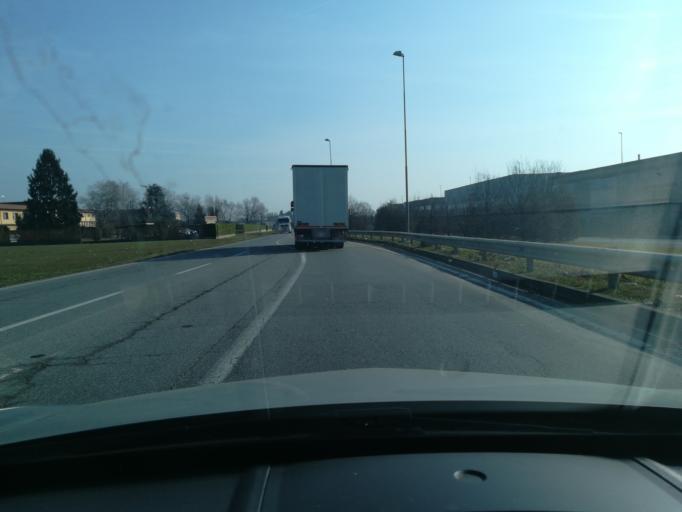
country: IT
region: Lombardy
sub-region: Provincia di Bergamo
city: Mornico al Serio
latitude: 45.5966
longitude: 9.8225
